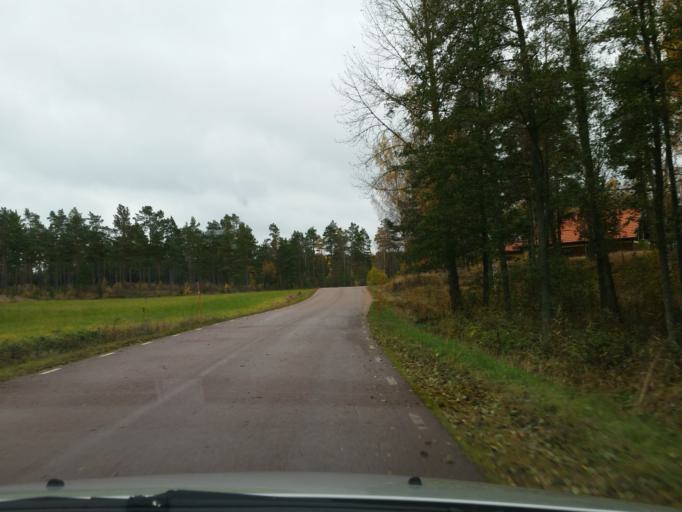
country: AX
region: Alands landsbygd
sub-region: Lumparland
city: Lumparland
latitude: 60.1334
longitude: 20.2738
